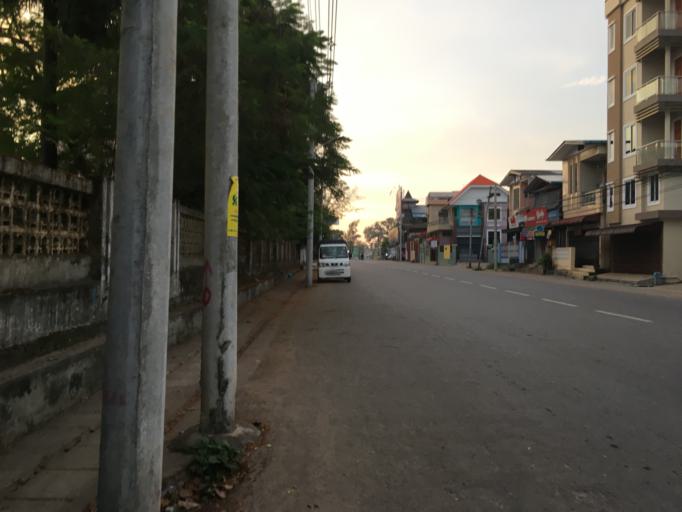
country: MM
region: Mon
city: Mawlamyine
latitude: 16.4702
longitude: 97.6258
